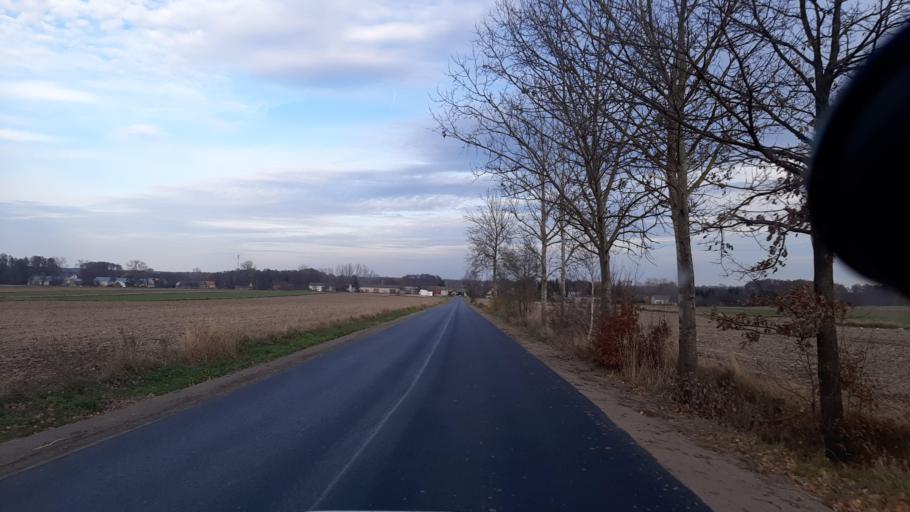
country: PL
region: Lublin Voivodeship
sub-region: Powiat lubelski
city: Garbow
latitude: 51.3873
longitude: 22.4053
